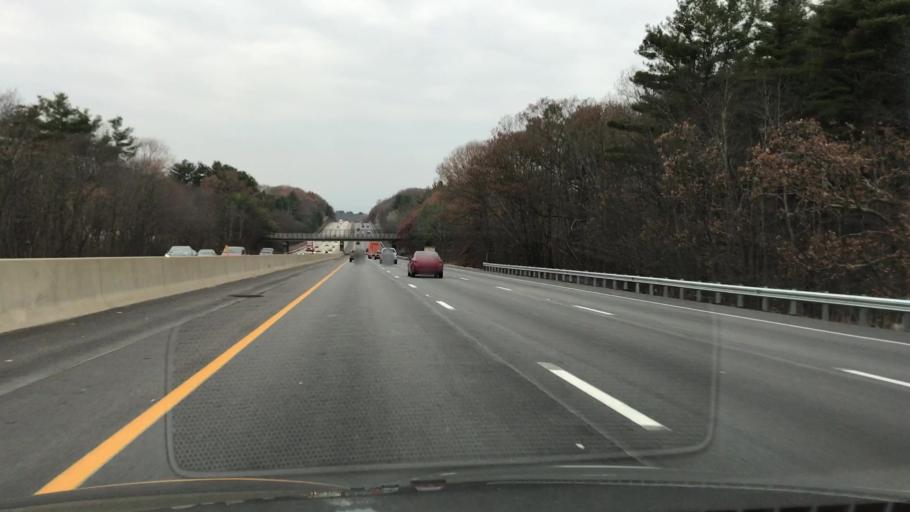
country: US
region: Massachusetts
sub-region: Worcester County
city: Grafton
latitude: 42.2272
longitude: -71.6786
